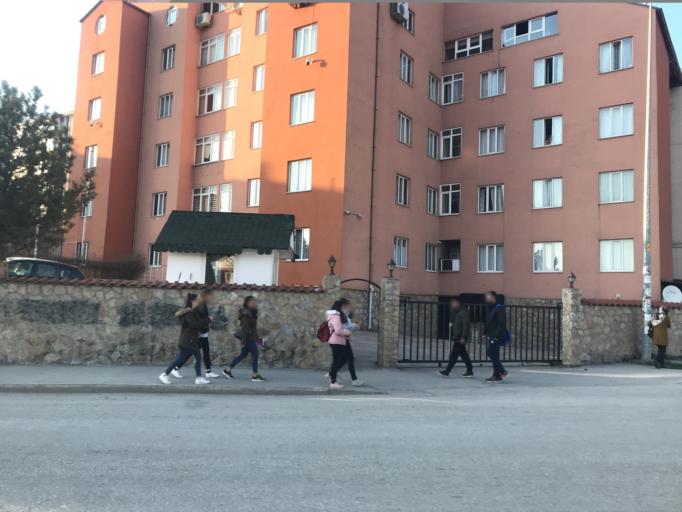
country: TR
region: Karabuk
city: Karabuk
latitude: 41.2183
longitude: 32.6668
